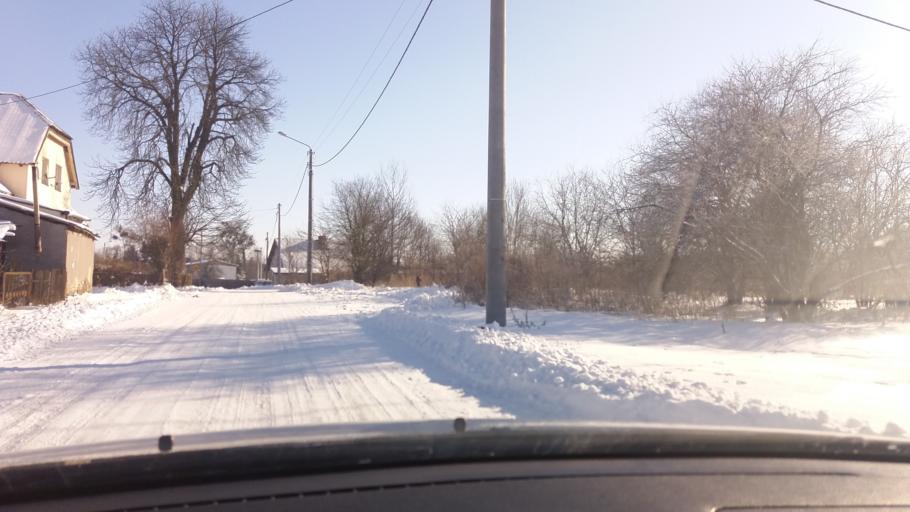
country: PL
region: Warmian-Masurian Voivodeship
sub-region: Powiat szczycienski
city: Szczytno
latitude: 53.5487
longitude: 20.9853
